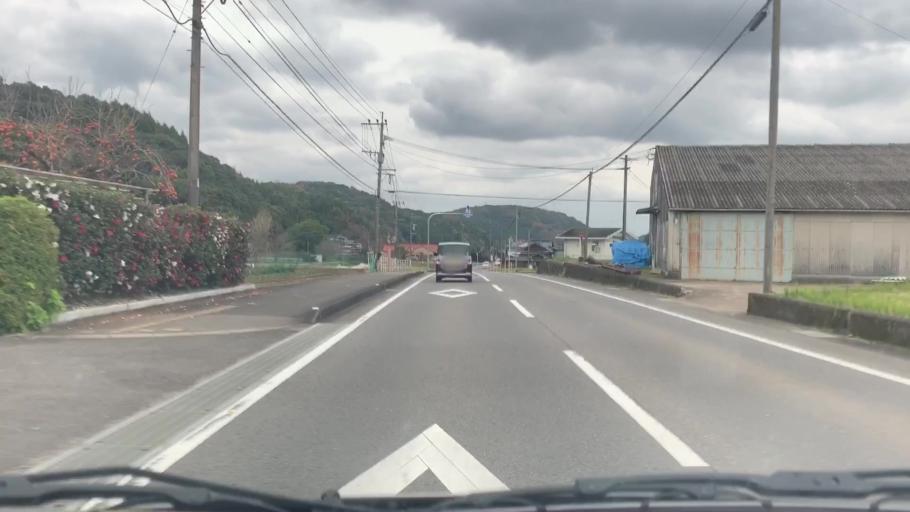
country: JP
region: Saga Prefecture
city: Kashima
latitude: 33.0990
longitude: 130.0542
